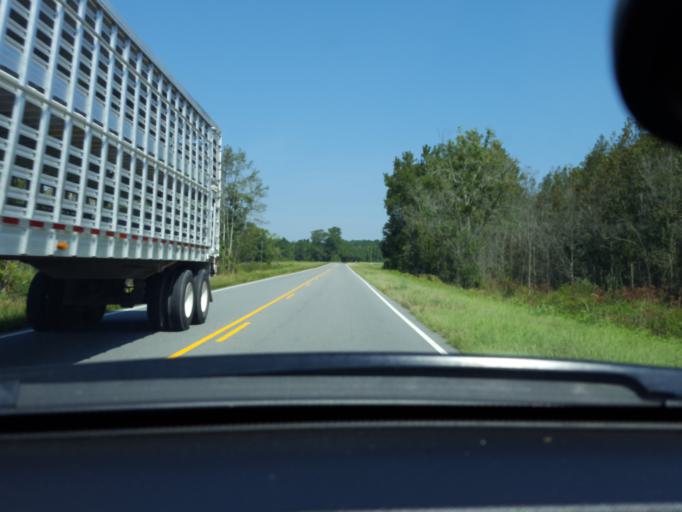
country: US
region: North Carolina
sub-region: Bladen County
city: Elizabethtown
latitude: 34.6772
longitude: -78.4900
